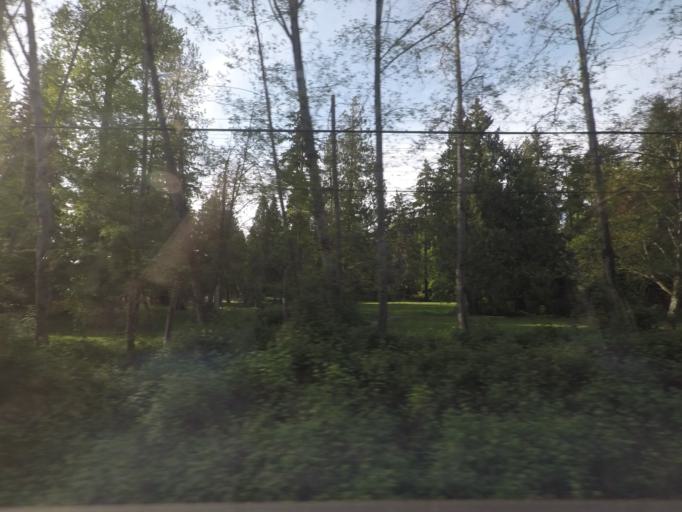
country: CA
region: British Columbia
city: Burnaby
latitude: 49.2458
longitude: -122.9338
